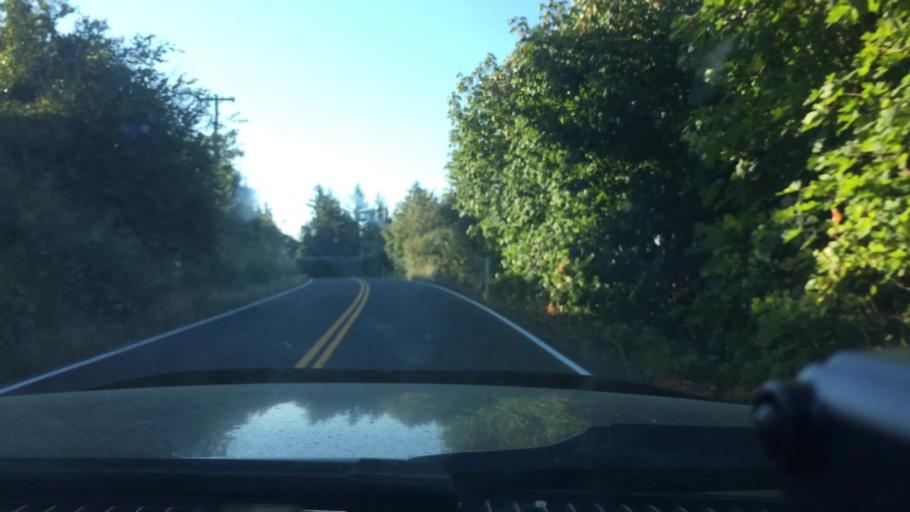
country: US
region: Oregon
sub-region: Yamhill County
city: Newberg
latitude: 45.3405
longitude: -122.9510
